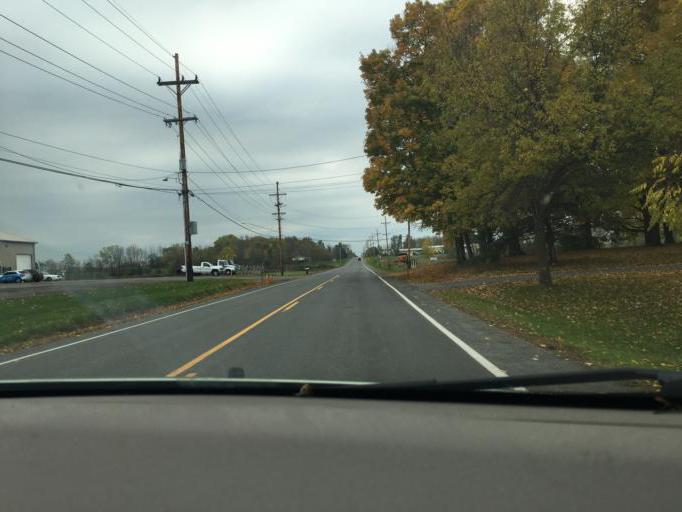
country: US
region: New York
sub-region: Ontario County
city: Manchester
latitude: 42.9720
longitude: -77.3191
